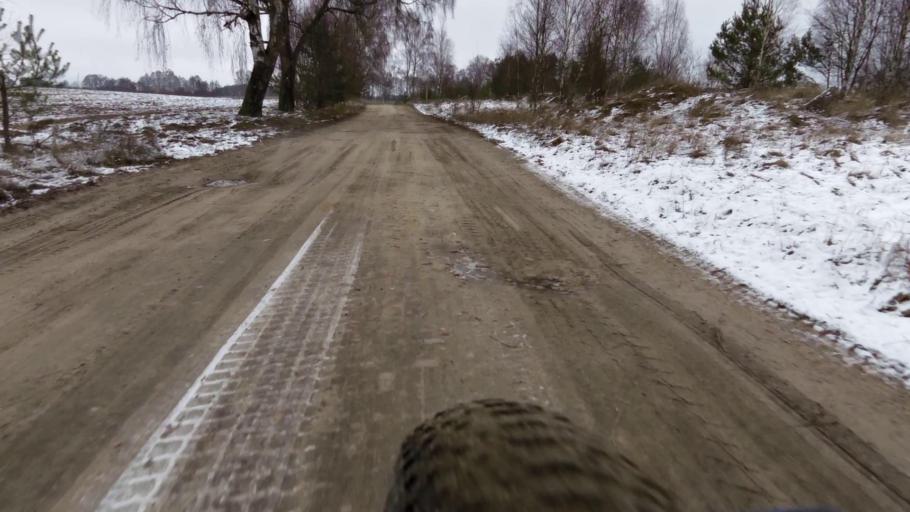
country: PL
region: West Pomeranian Voivodeship
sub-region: Powiat walecki
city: Miroslawiec
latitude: 53.3187
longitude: 16.0794
